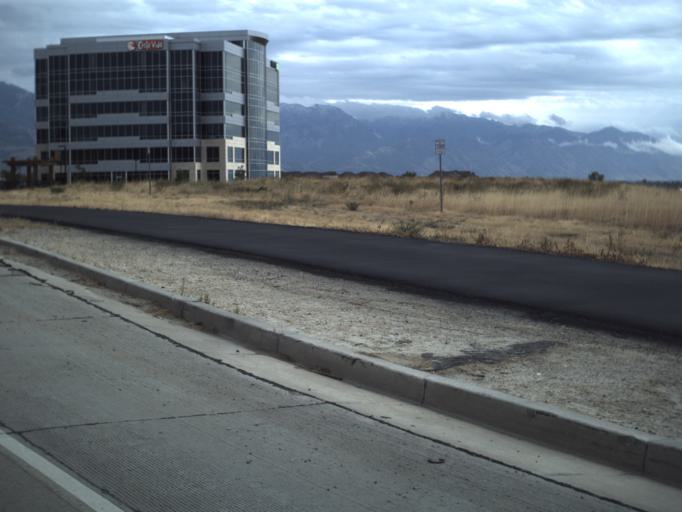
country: US
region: Utah
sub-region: Utah County
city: Lehi
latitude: 40.4314
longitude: -111.8849
